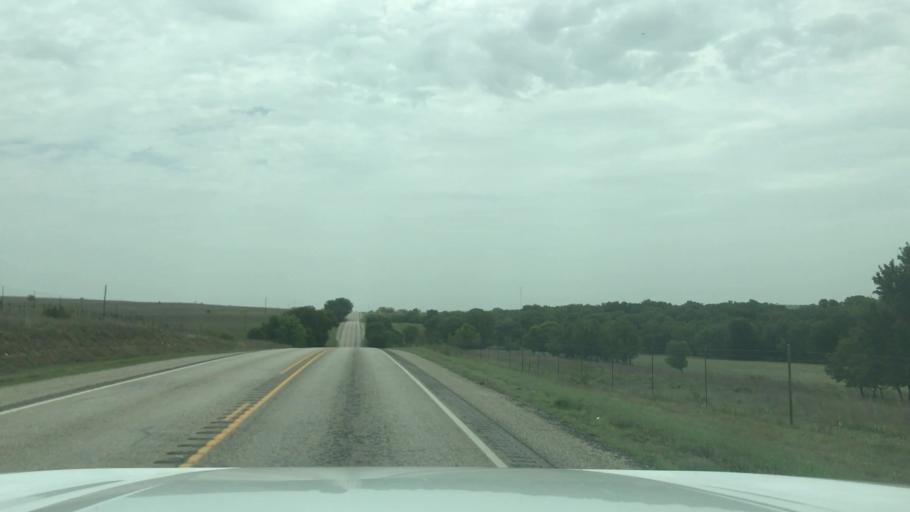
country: US
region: Texas
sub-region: Erath County
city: Dublin
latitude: 32.0558
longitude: -98.1814
